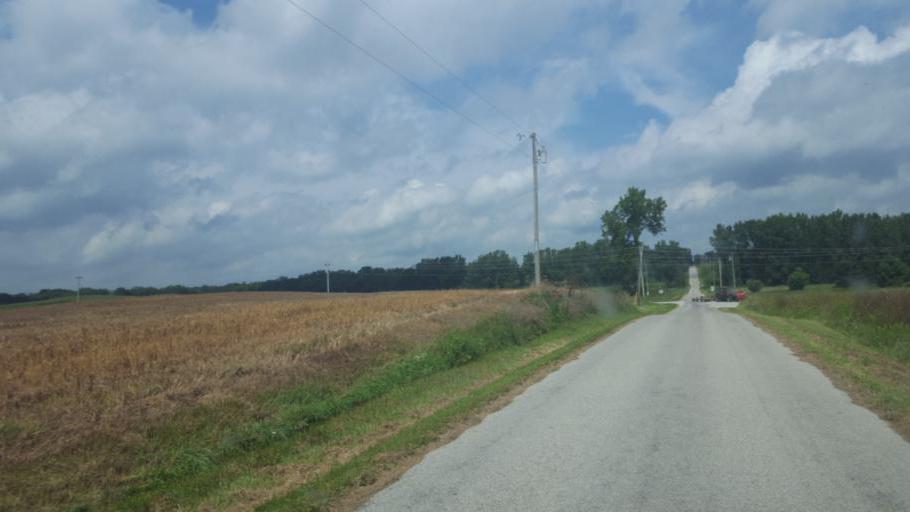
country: US
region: Ohio
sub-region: Richland County
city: Lexington
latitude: 40.6513
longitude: -82.6899
